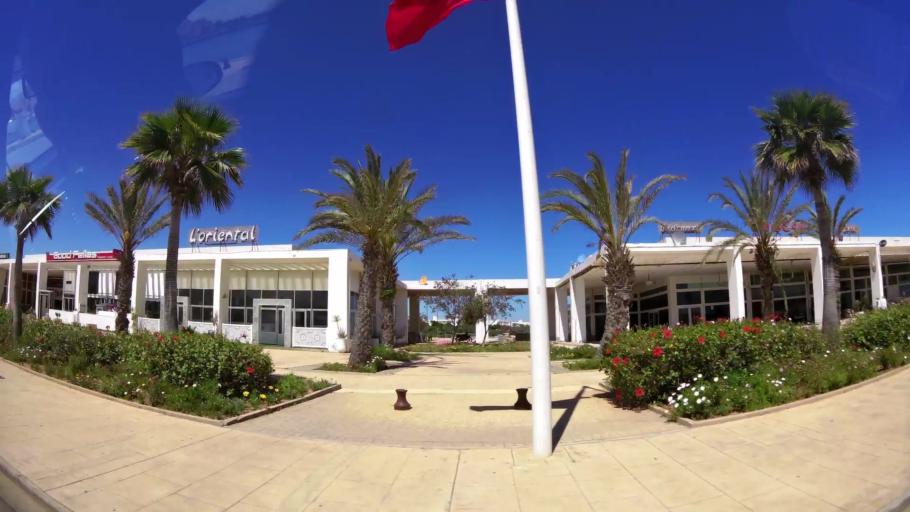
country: MA
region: Oriental
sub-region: Berkane-Taourirt
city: Madagh
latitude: 35.1103
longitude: -2.2979
